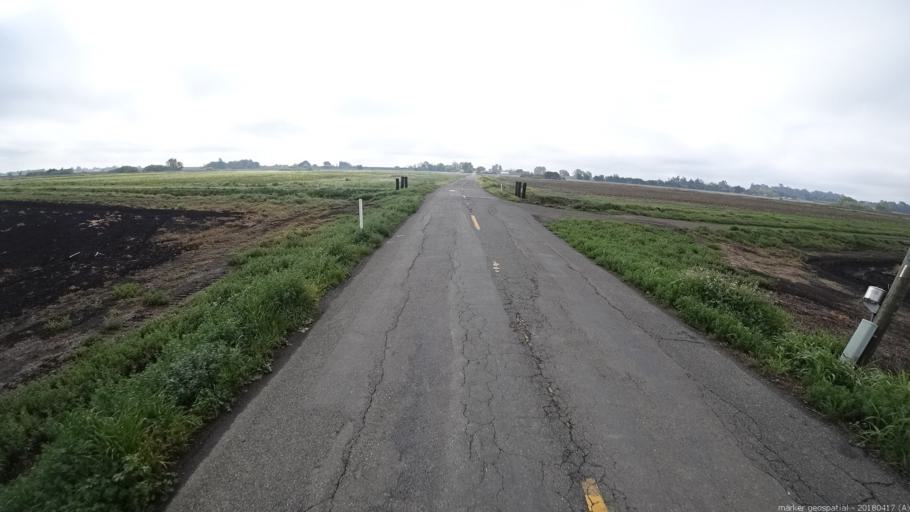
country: US
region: California
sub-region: Sacramento County
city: Walnut Grove
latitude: 38.1894
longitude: -121.5927
